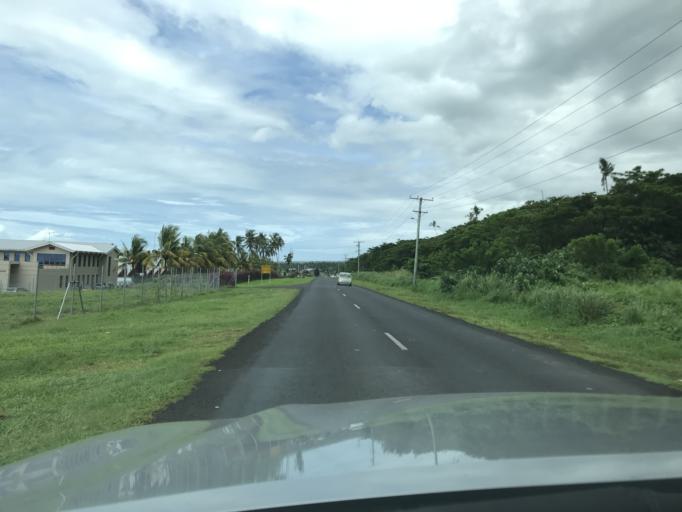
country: WS
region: A'ana
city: Satapuala
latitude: -13.8338
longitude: -172.0004
